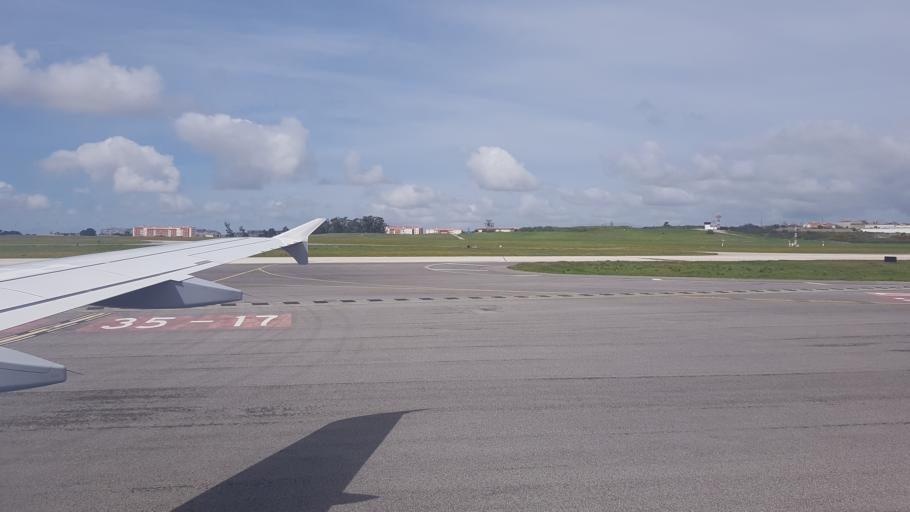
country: PT
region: Lisbon
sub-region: Loures
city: Camarate
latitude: 38.7765
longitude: -9.1332
